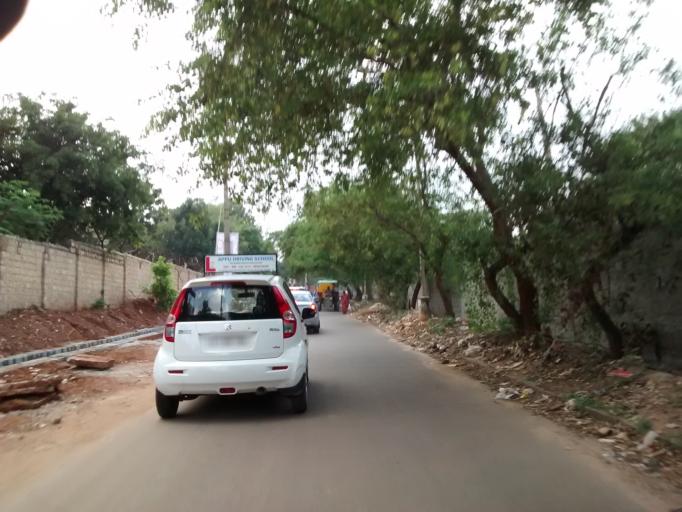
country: IN
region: Karnataka
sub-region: Bangalore Urban
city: Bangalore
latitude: 12.9628
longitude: 77.6685
